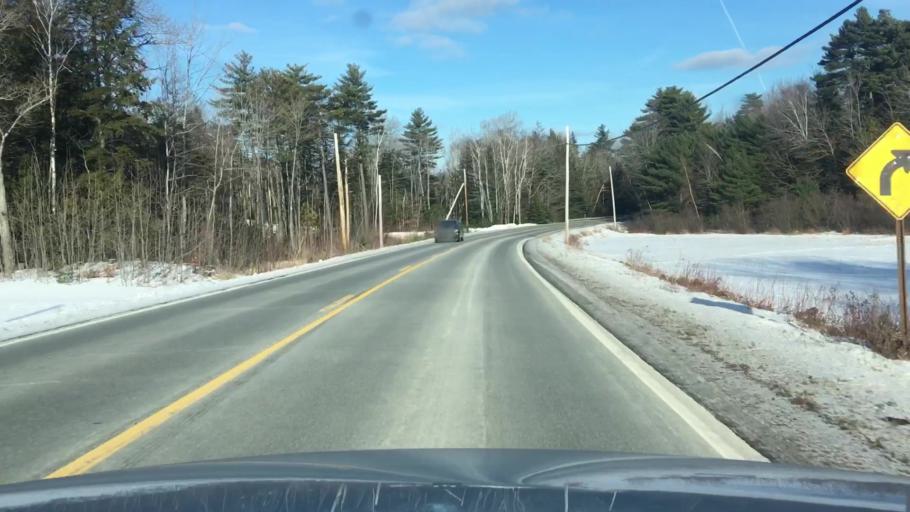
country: US
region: Maine
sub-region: Penobscot County
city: Holden
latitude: 44.7504
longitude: -68.6114
